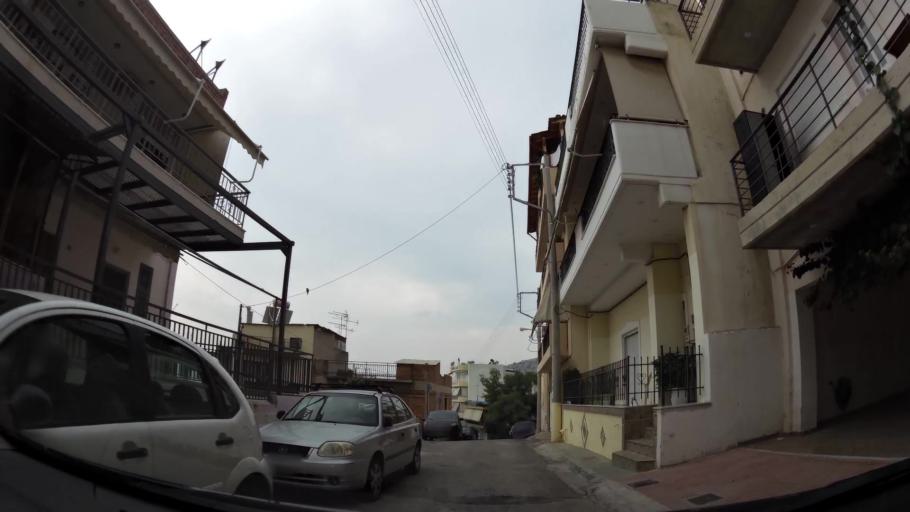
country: GR
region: Attica
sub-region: Nomos Piraios
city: Keratsini
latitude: 37.9798
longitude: 23.6278
